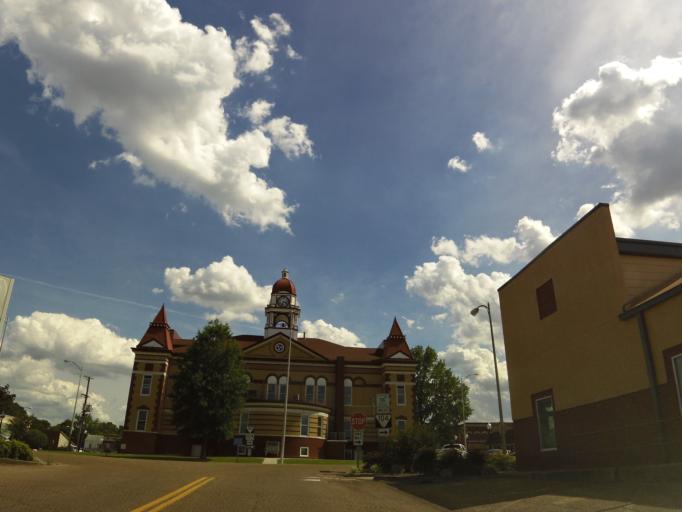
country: US
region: Tennessee
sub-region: Gibson County
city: Trenton
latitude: 35.9819
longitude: -88.9416
